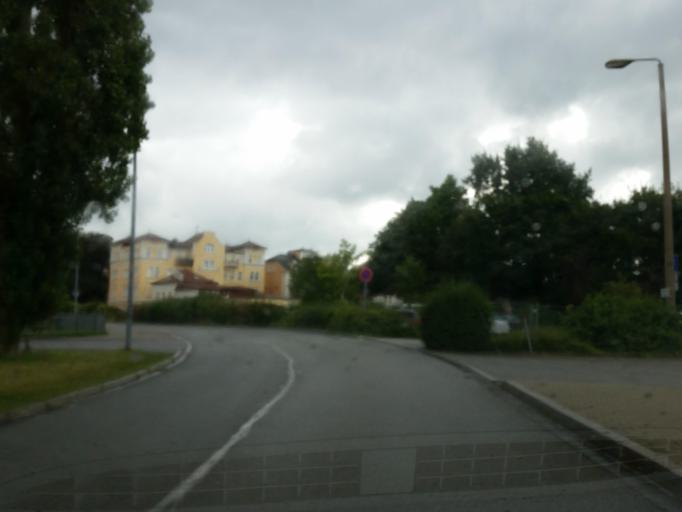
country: DE
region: Saxony
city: Bautzen
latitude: 51.1853
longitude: 14.4250
